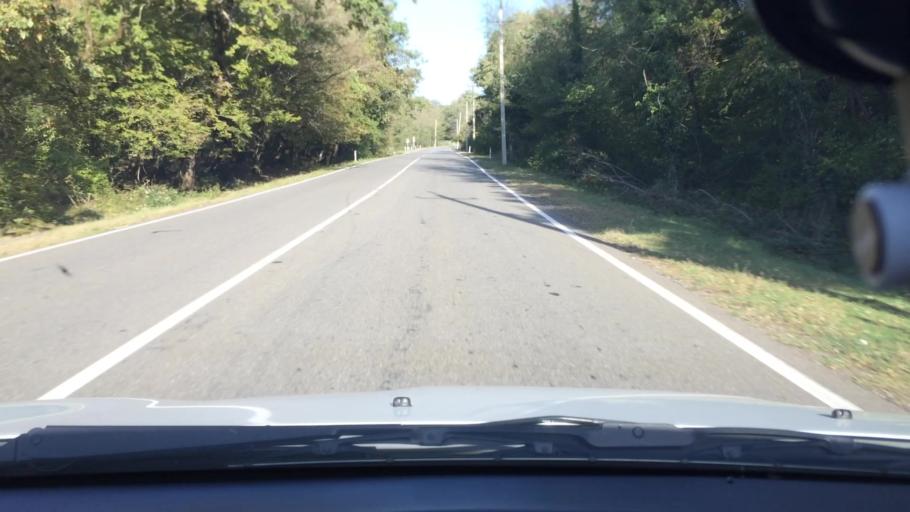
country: GE
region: Imereti
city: Kutaisi
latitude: 42.2460
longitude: 42.7582
